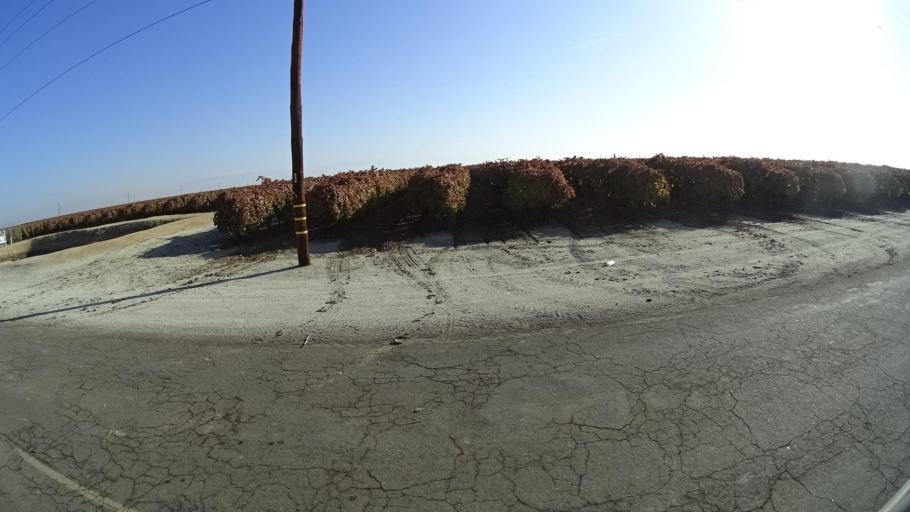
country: US
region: California
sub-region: Tulare County
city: Richgrove
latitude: 35.7589
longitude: -119.1696
